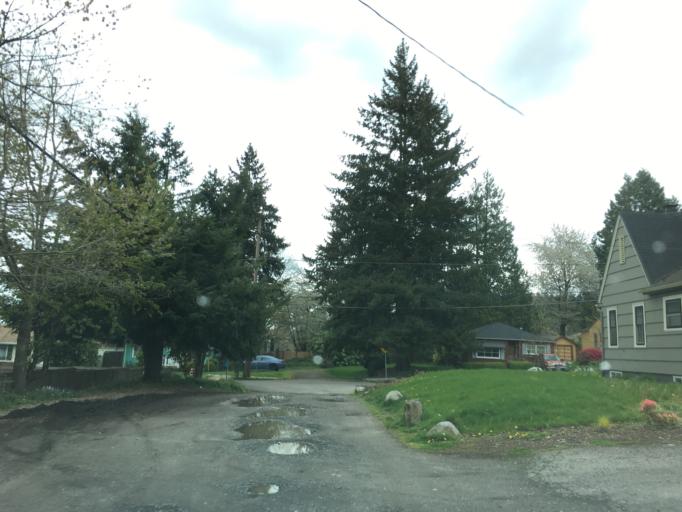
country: US
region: Oregon
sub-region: Multnomah County
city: Lents
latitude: 45.5538
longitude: -122.5823
